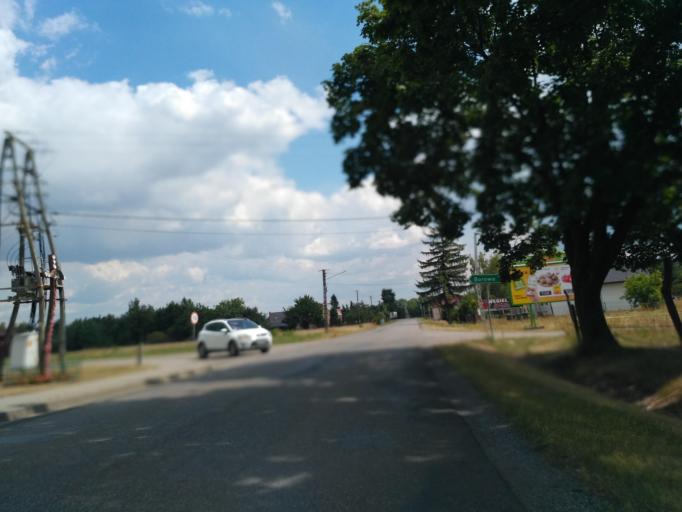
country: PL
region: Subcarpathian Voivodeship
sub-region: Powiat debicki
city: Pilzno
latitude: 50.0316
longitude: 21.3072
